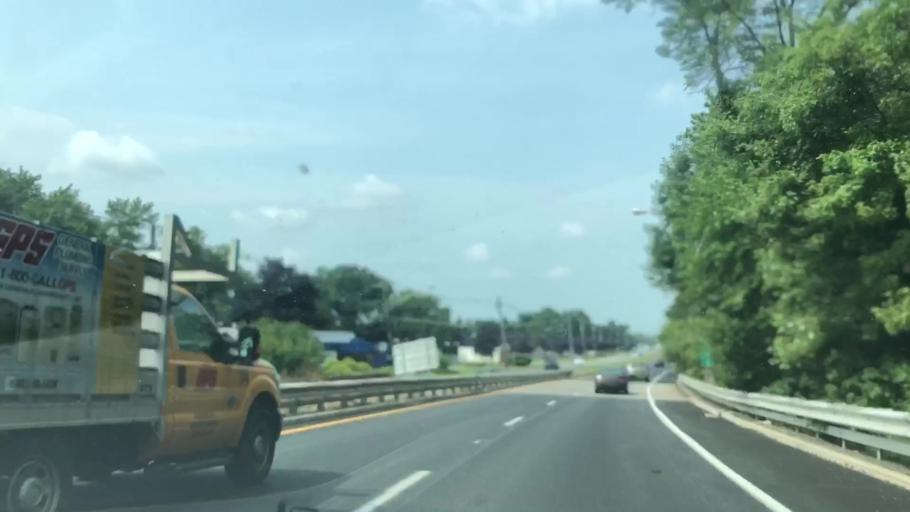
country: US
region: New Jersey
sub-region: Essex County
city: Westville
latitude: 40.8594
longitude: -74.3270
